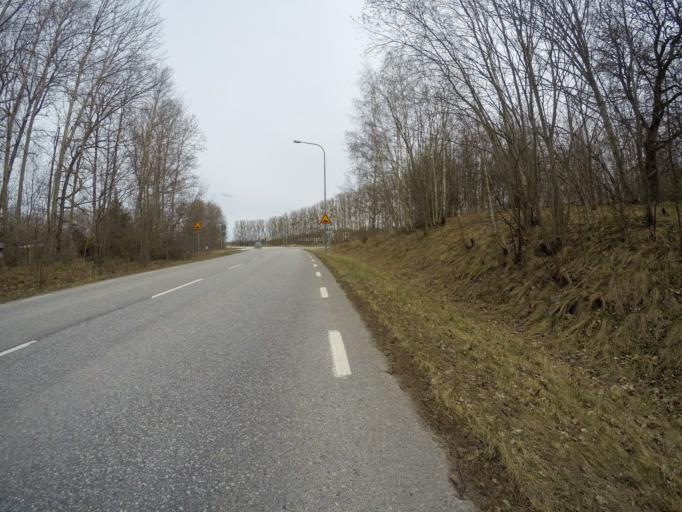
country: SE
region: Vaestmanland
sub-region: Vasteras
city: Vasteras
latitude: 59.5936
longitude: 16.6107
